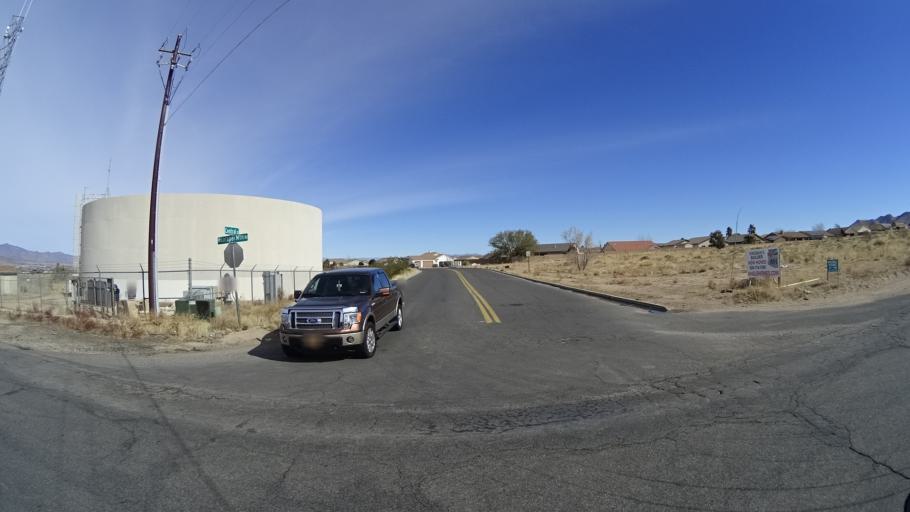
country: US
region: Arizona
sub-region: Mohave County
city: Kingman
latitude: 35.1844
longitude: -114.0034
